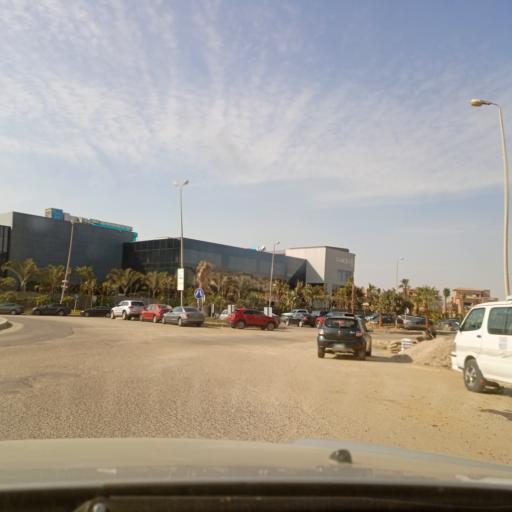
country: EG
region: Muhafazat al Qalyubiyah
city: Al Khankah
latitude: 30.0459
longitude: 31.4855
